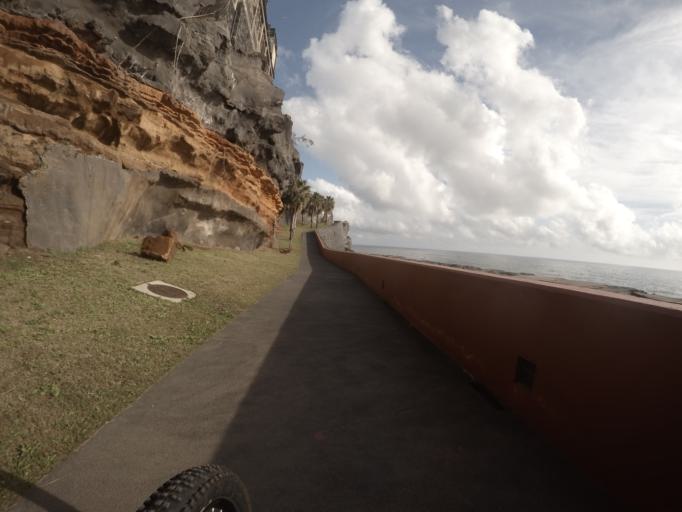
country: PT
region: Madeira
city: Camara de Lobos
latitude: 32.6458
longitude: -16.9726
